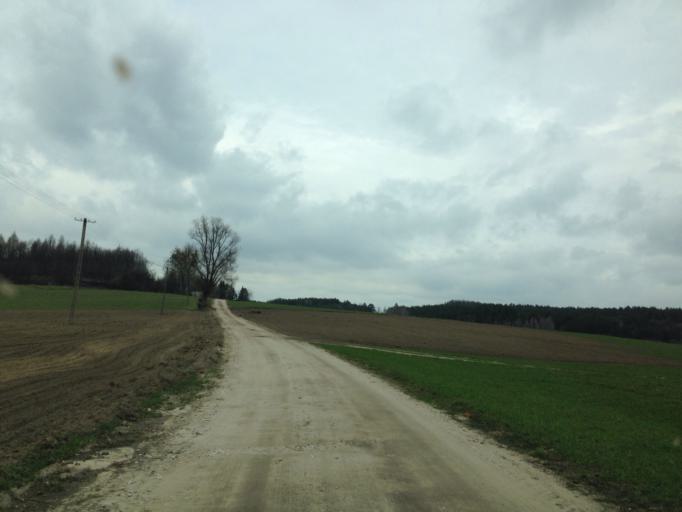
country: PL
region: Warmian-Masurian Voivodeship
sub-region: Powiat dzialdowski
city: Lidzbark
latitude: 53.2127
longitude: 19.7453
